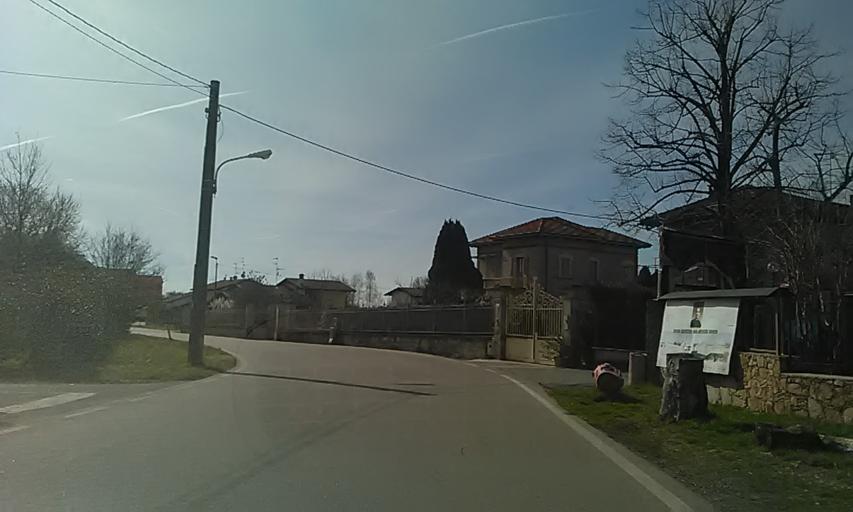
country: IT
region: Piedmont
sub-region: Provincia di Biella
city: Brusnengo
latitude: 45.5964
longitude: 8.2488
